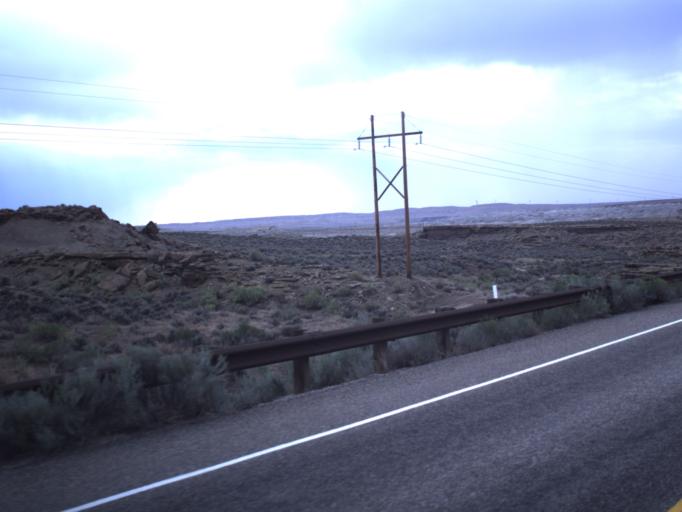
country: US
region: Colorado
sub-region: Rio Blanco County
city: Rangely
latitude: 40.0872
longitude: -109.2192
